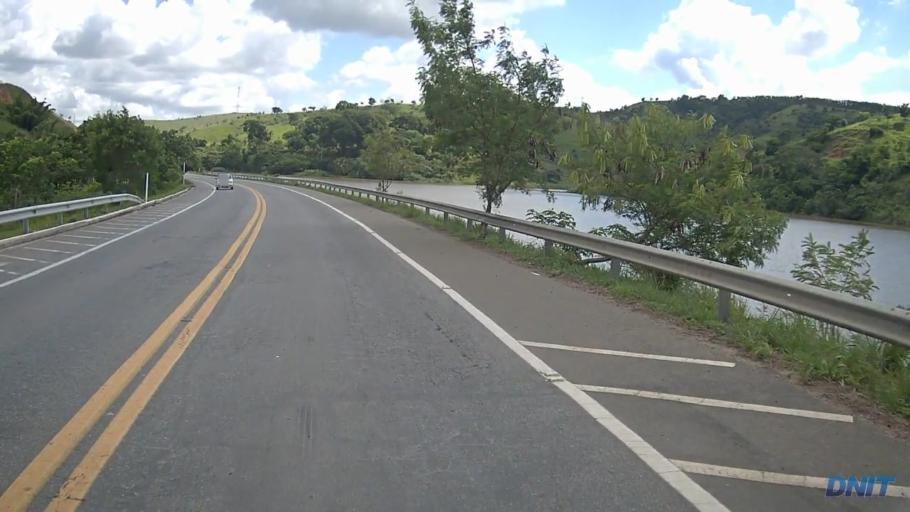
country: BR
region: Minas Gerais
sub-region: Governador Valadares
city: Governador Valadares
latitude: -19.0388
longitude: -42.1481
